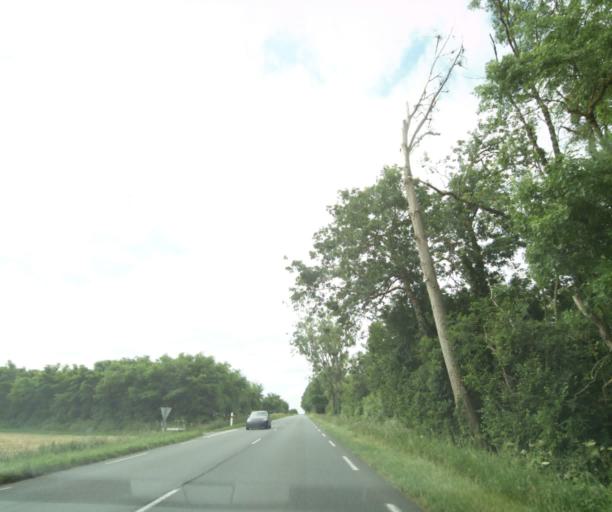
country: FR
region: Pays de la Loire
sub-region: Departement de Maine-et-Loire
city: Montreuil-Bellay
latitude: 47.0923
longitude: -0.1709
